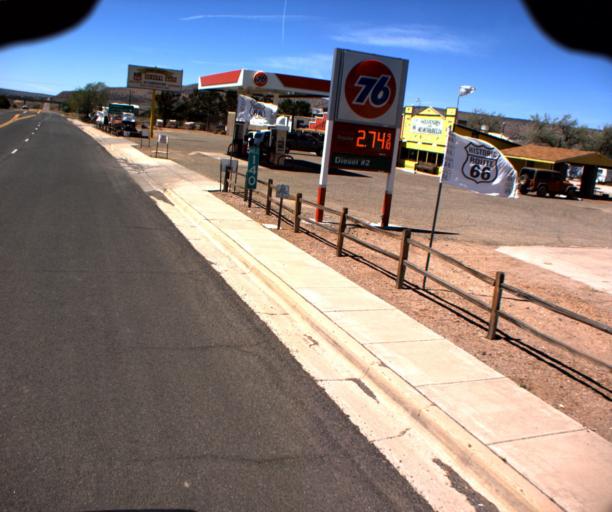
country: US
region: Arizona
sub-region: Mohave County
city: Peach Springs
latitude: 35.3287
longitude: -112.8845
